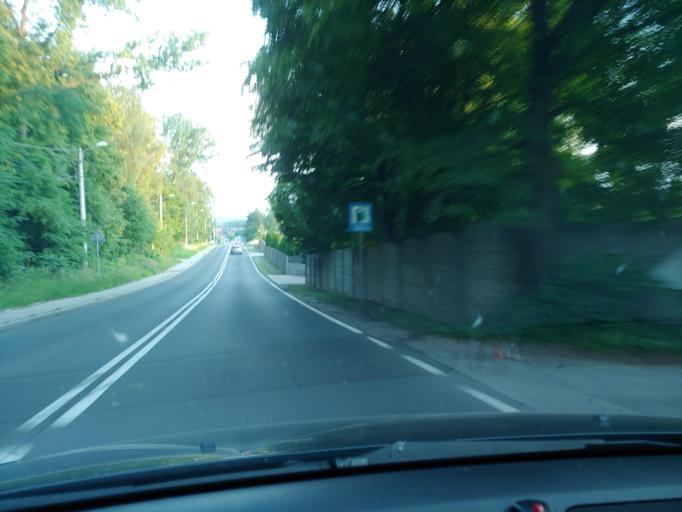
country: PL
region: Lesser Poland Voivodeship
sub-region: Powiat chrzanowski
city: Myslachowice
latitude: 50.1763
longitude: 19.4737
